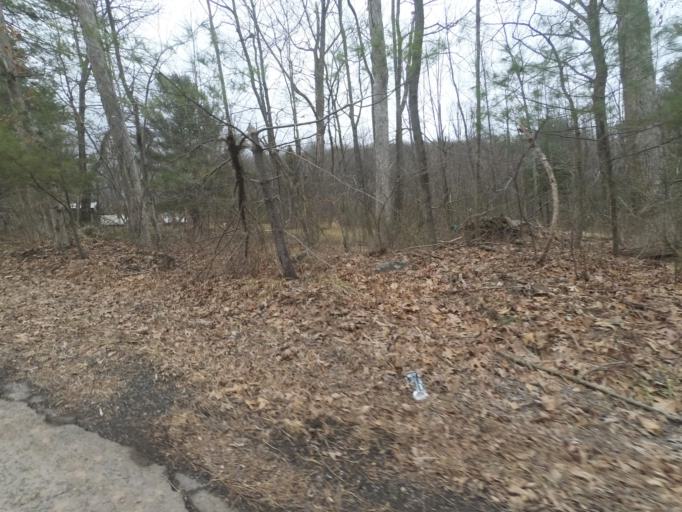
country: US
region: Pennsylvania
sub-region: Centre County
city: Stormstown
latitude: 40.8704
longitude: -78.0093
